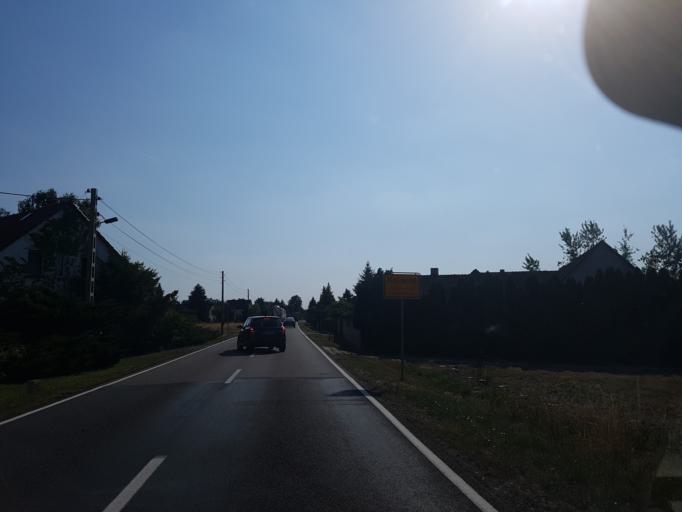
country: DE
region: Saxony-Anhalt
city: Annaburg
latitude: 51.7075
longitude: 13.0214
